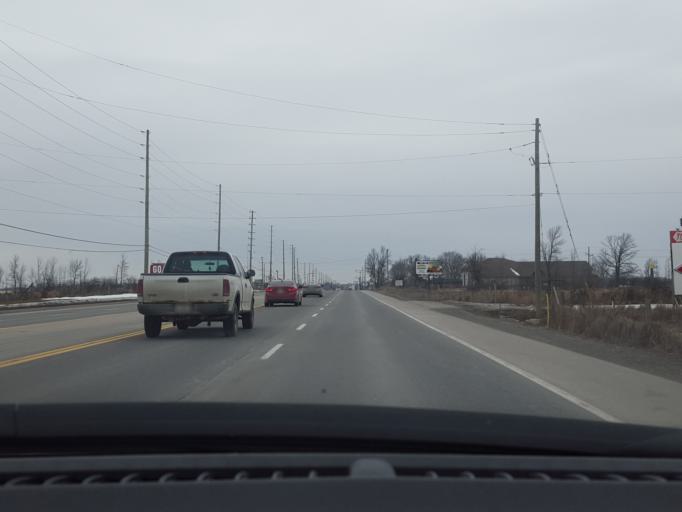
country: CA
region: Ontario
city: Keswick
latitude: 44.2126
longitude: -79.4432
